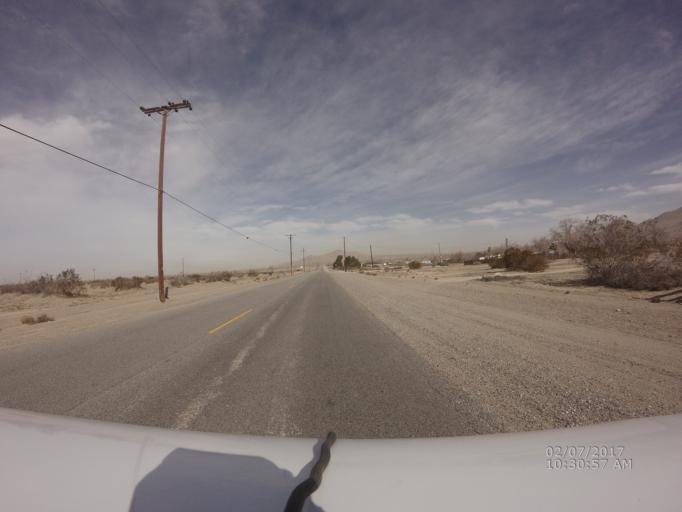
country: US
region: California
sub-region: Los Angeles County
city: Lake Los Angeles
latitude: 34.6664
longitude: -117.8275
